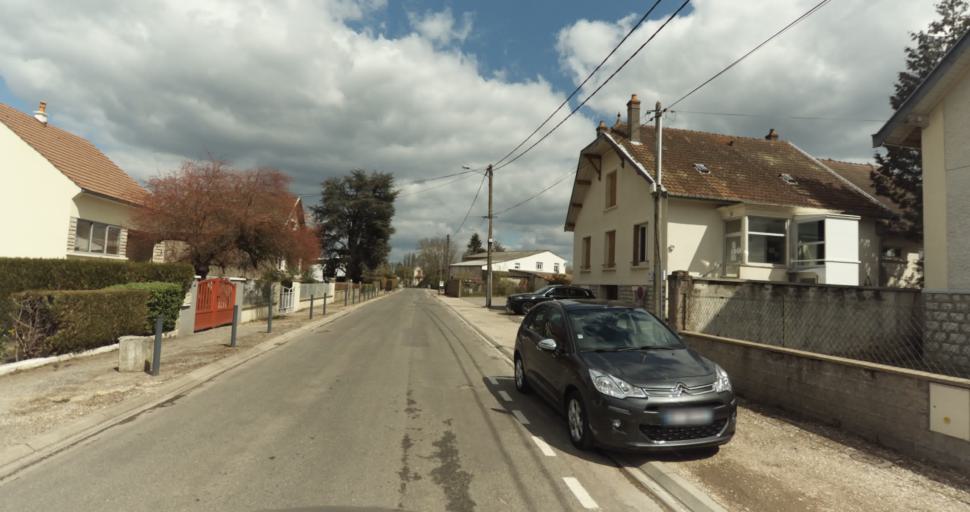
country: FR
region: Bourgogne
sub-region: Departement de la Cote-d'Or
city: Auxonne
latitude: 47.1894
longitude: 5.3920
